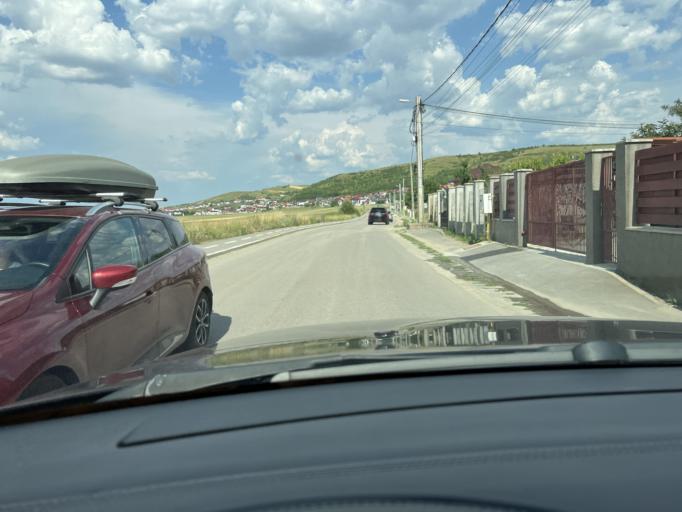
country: RO
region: Cluj
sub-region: Comuna Apahida
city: Sannicoara
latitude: 46.7782
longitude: 23.7122
